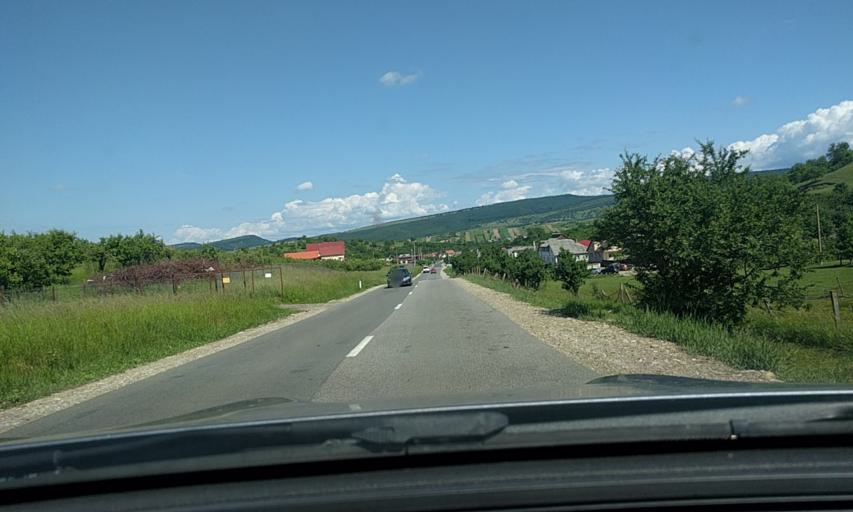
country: RO
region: Bistrita-Nasaud
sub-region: Comuna Dumitra
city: Dumitra
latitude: 47.2103
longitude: 24.4706
